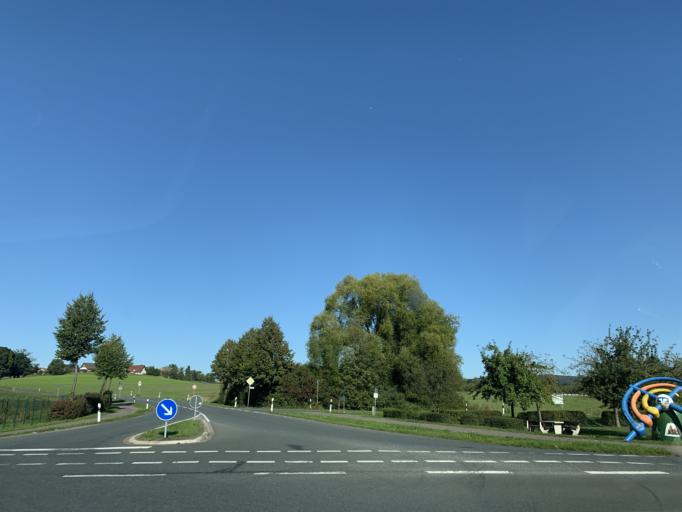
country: DE
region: North Rhine-Westphalia
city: Porta Westfalica
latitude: 52.1958
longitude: 8.9795
